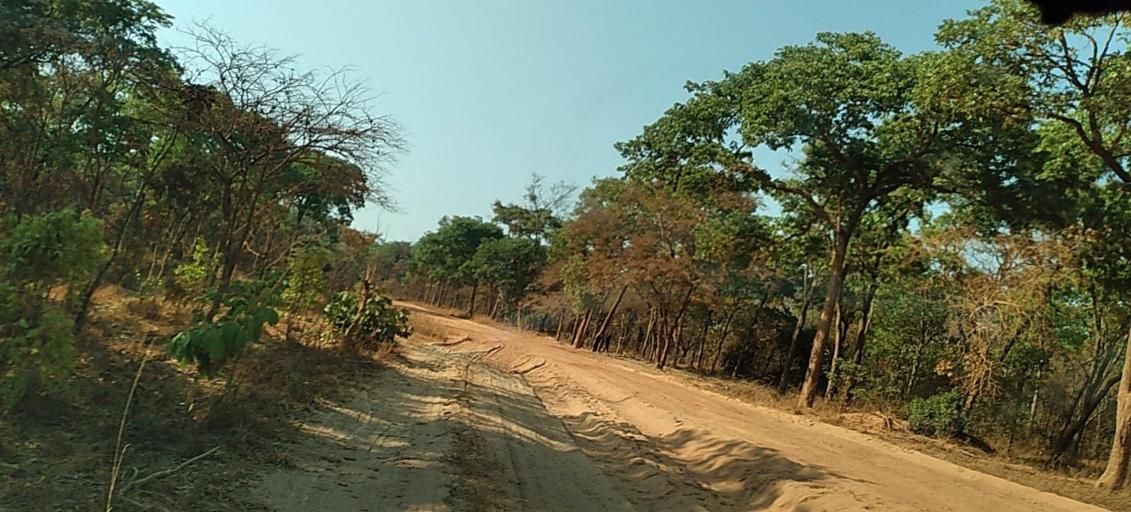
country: ZM
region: North-Western
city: Kasempa
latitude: -13.6636
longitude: 26.0110
